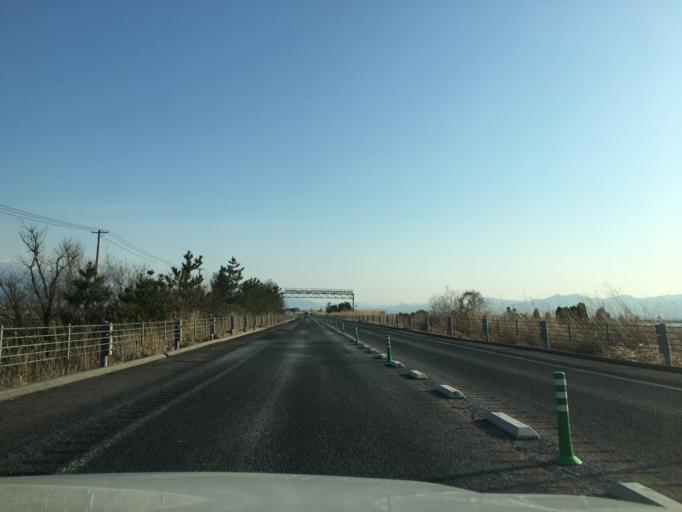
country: JP
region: Yamagata
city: Sagae
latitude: 38.3319
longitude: 140.2974
